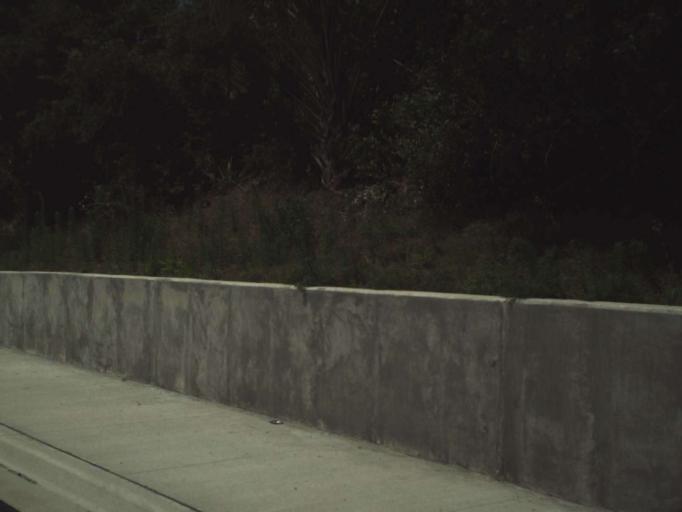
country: US
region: Florida
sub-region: Seminole County
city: Midway
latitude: 28.8648
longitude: -81.1624
